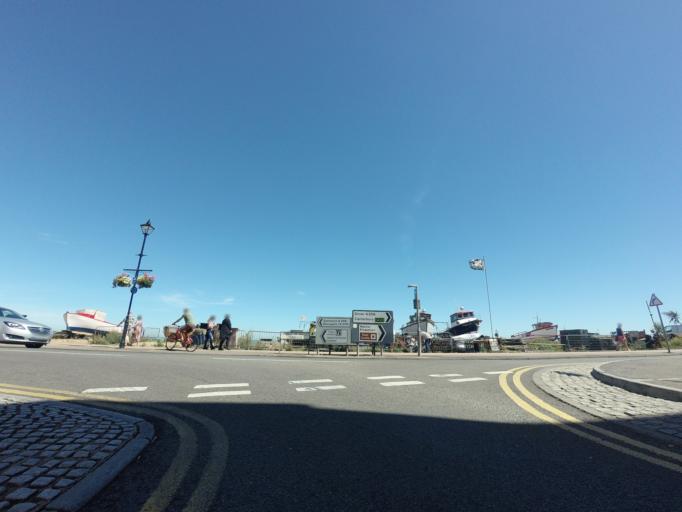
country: GB
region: England
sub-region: Kent
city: Deal
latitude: 51.2204
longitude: 1.4044
